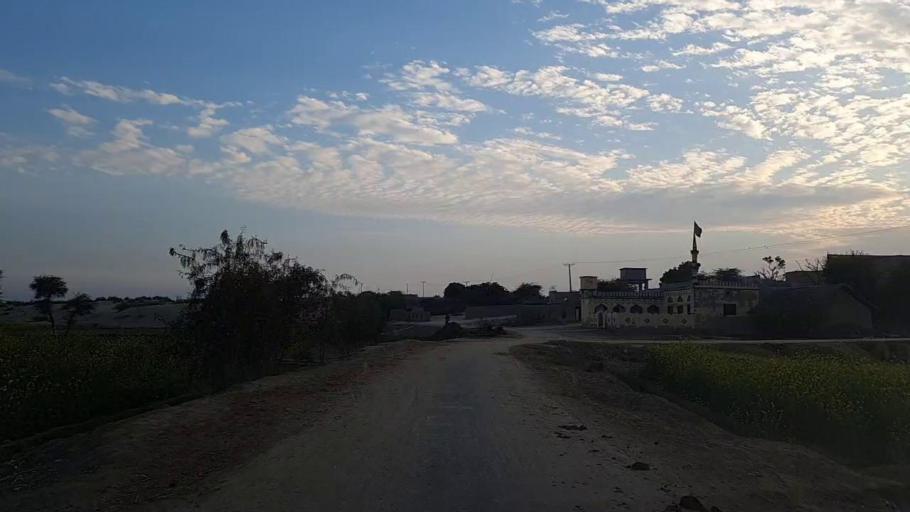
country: PK
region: Sindh
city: Daur
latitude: 26.4130
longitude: 68.4678
